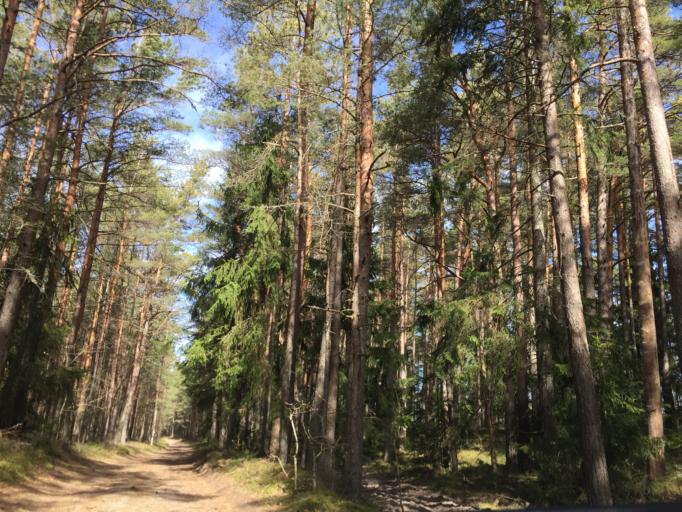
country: LV
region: Salacgrivas
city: Salacgriva
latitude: 57.6919
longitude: 24.3606
